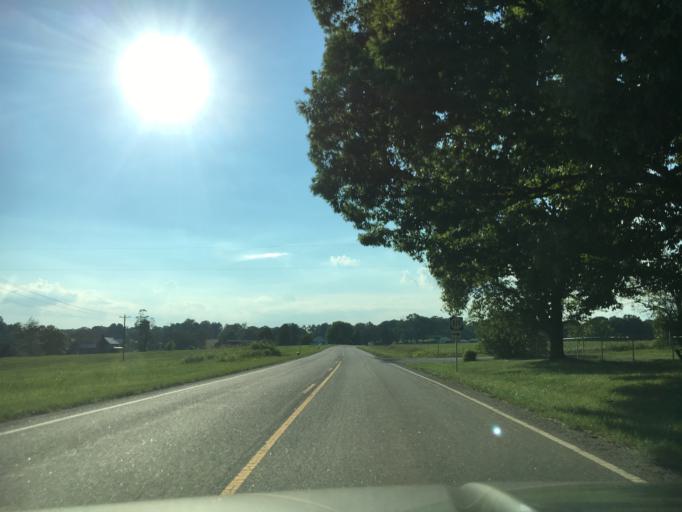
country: US
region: Virginia
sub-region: City of Bedford
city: Bedford
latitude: 37.2278
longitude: -79.5257
